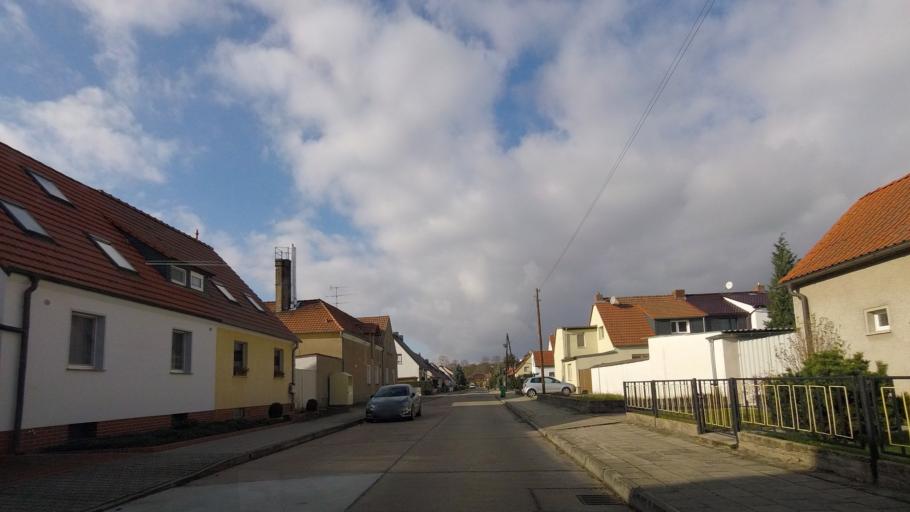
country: DE
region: Brandenburg
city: Juterbog
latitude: 51.9944
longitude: 13.0623
